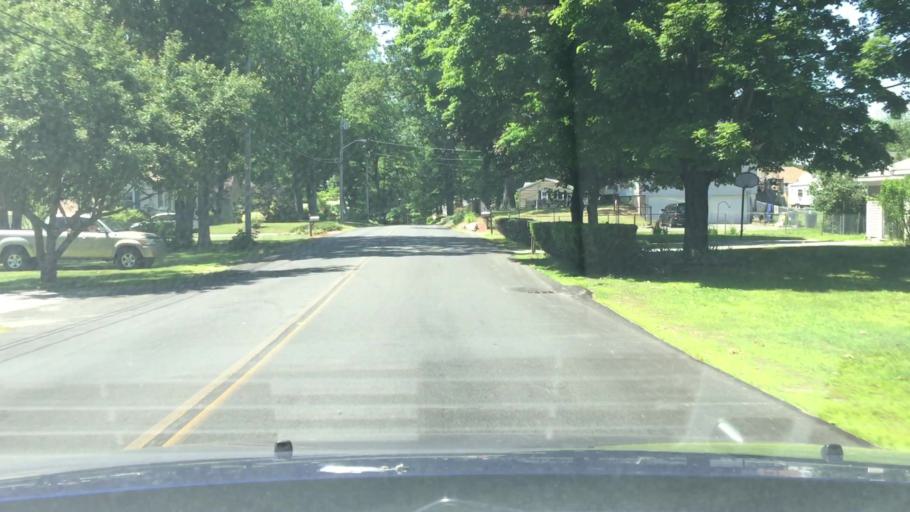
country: US
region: New Hampshire
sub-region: Rockingham County
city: Plaistow
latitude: 42.8190
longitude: -71.0970
